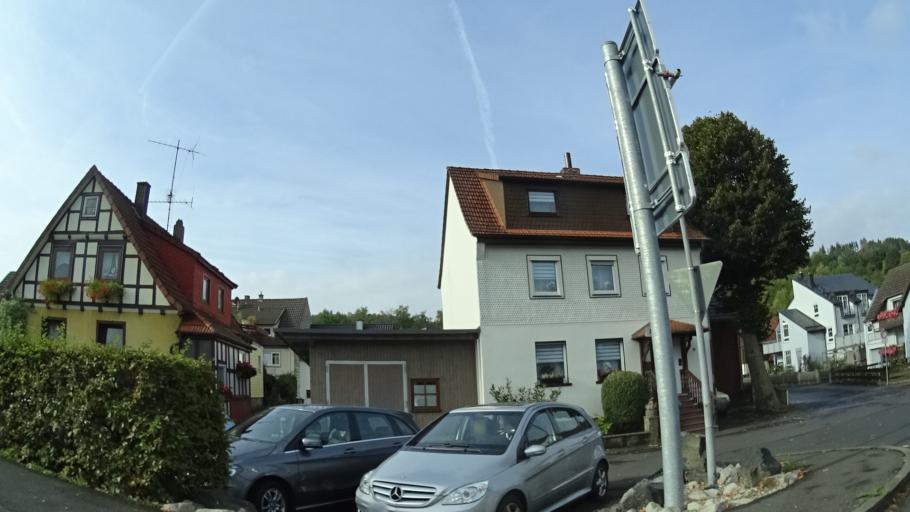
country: DE
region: Hesse
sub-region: Regierungsbezirk Kassel
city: Hilders
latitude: 50.5723
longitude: 9.9991
